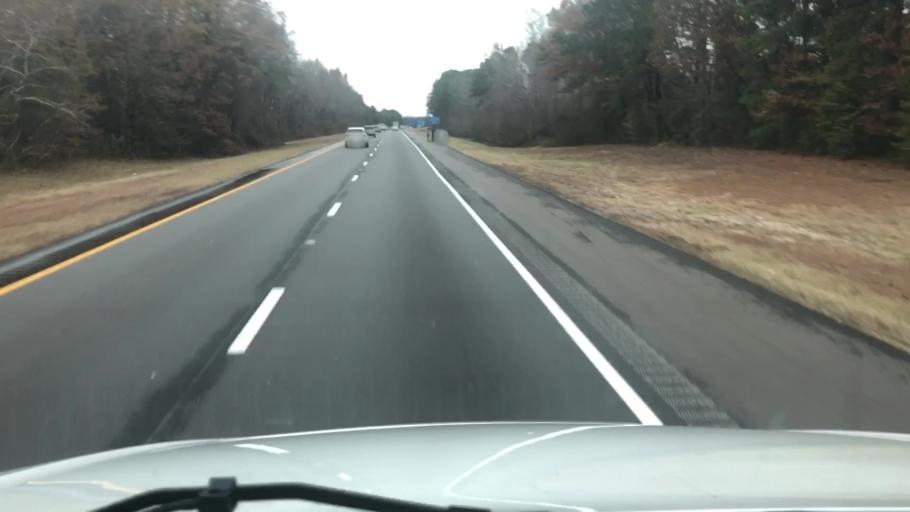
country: US
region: North Carolina
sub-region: Cumberland County
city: Eastover
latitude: 35.0676
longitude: -78.7924
